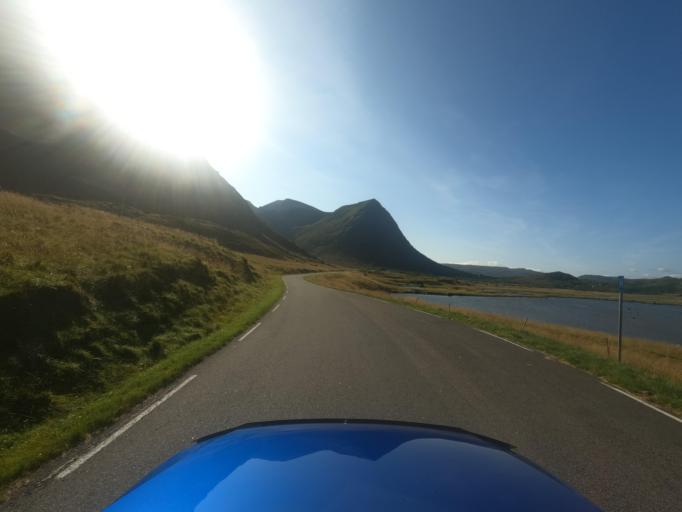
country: NO
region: Nordland
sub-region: Vestvagoy
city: Evjen
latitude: 68.3297
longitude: 13.9186
